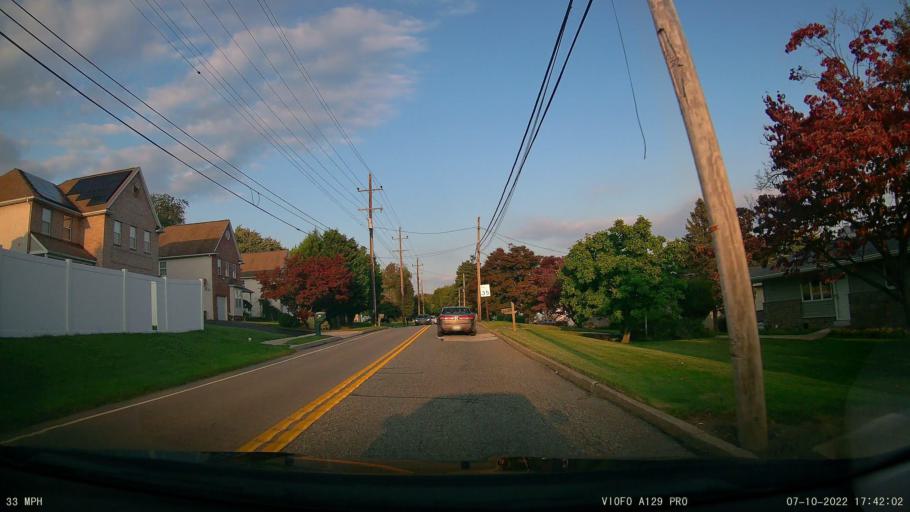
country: US
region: Pennsylvania
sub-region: Montgomery County
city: Bridgeport
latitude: 40.1027
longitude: -75.3670
